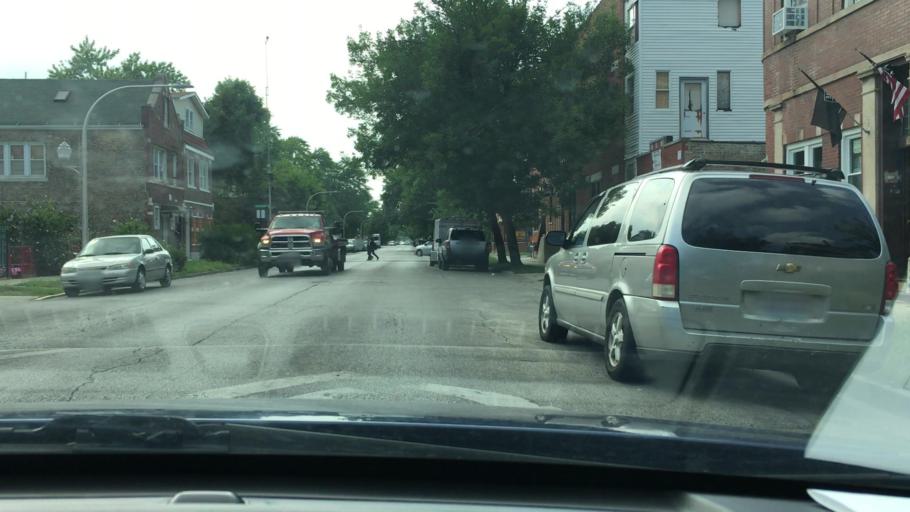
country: US
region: Illinois
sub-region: Cook County
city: Chicago
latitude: 41.8465
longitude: -87.6920
